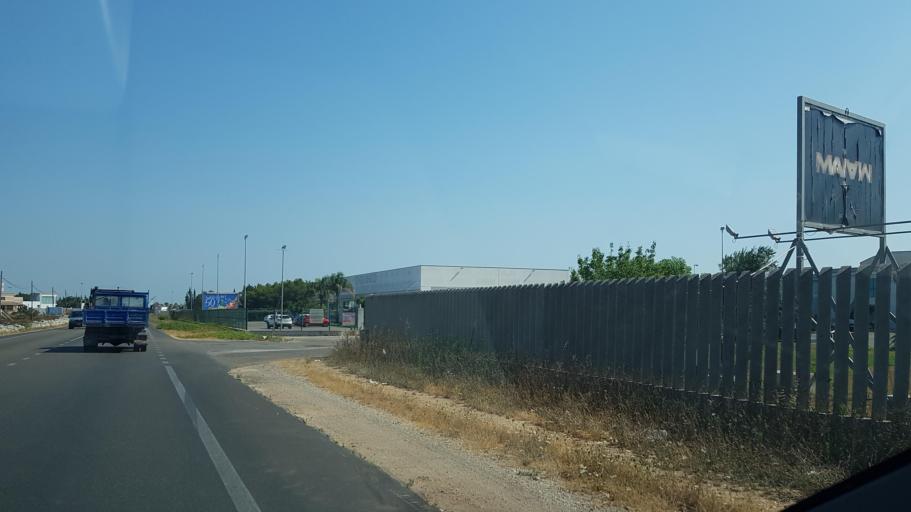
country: IT
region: Apulia
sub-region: Provincia di Lecce
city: Nociglia
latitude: 40.0155
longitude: 18.3243
